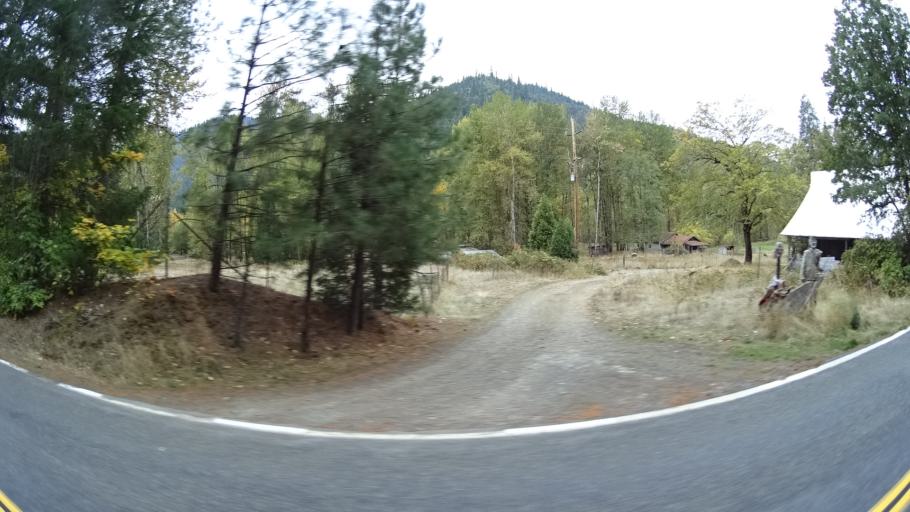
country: US
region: California
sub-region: Siskiyou County
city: Happy Camp
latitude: 41.8705
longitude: -123.4057
